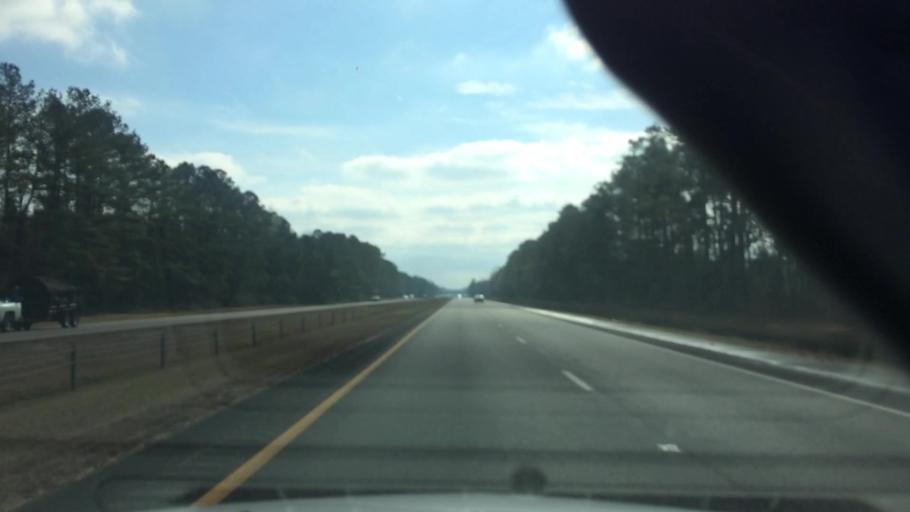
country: US
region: North Carolina
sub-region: Pender County
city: Rocky Point
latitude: 34.4932
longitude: -77.8775
